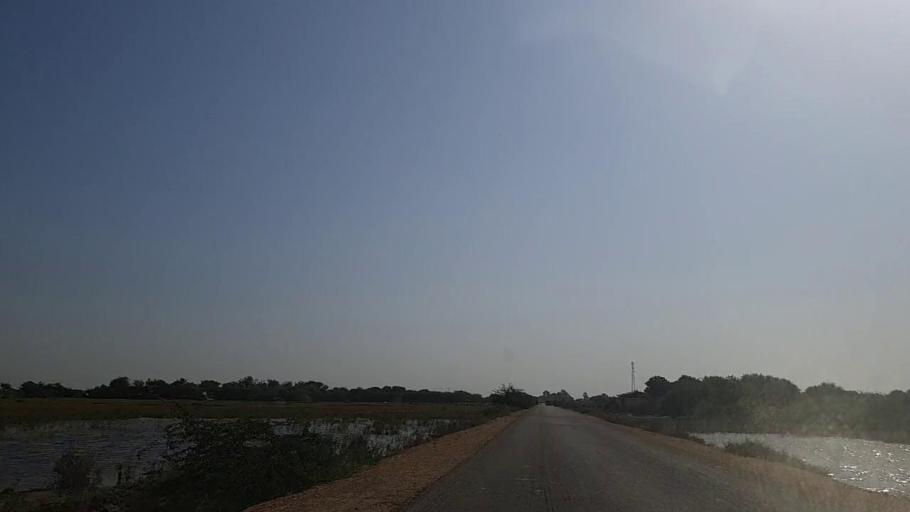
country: PK
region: Sindh
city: Jati
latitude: 24.5233
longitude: 68.2766
